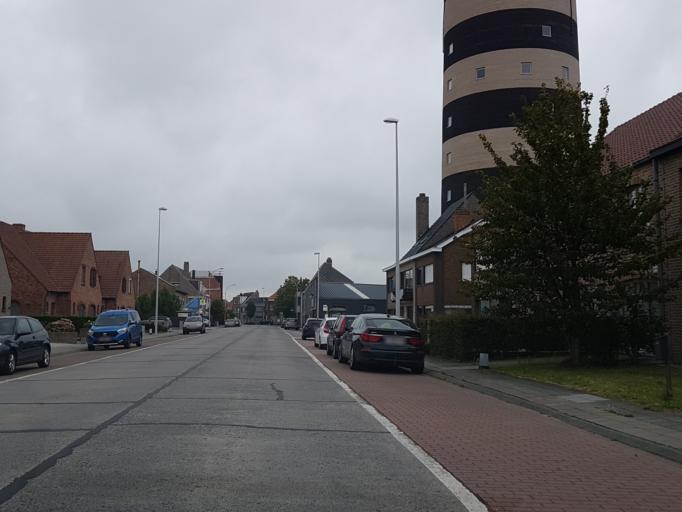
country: BE
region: Flanders
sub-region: Provincie West-Vlaanderen
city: Bredene
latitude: 51.2333
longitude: 2.9709
